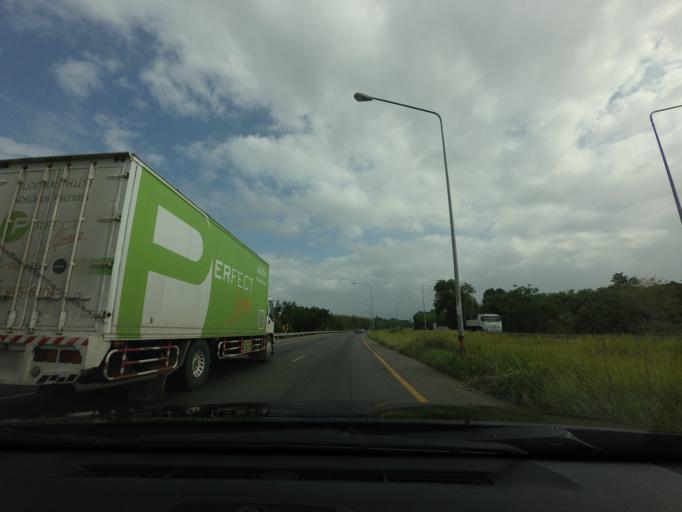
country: TH
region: Pattani
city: Mae Lan
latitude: 6.6258
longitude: 101.2340
